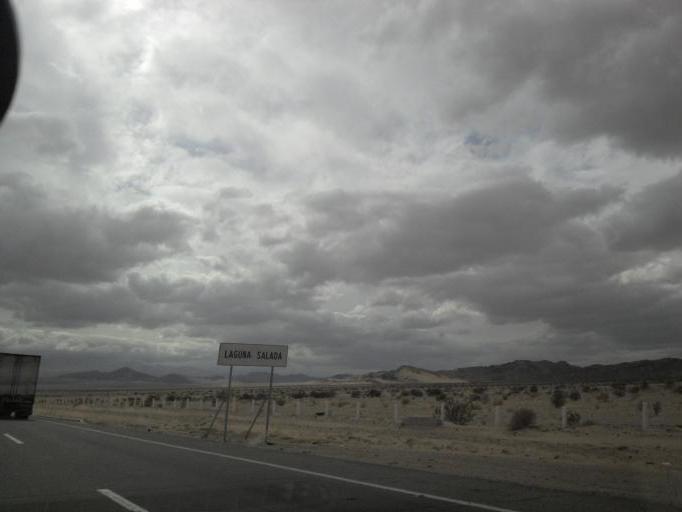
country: MX
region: Baja California
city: Progreso
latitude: 32.5771
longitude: -115.7379
